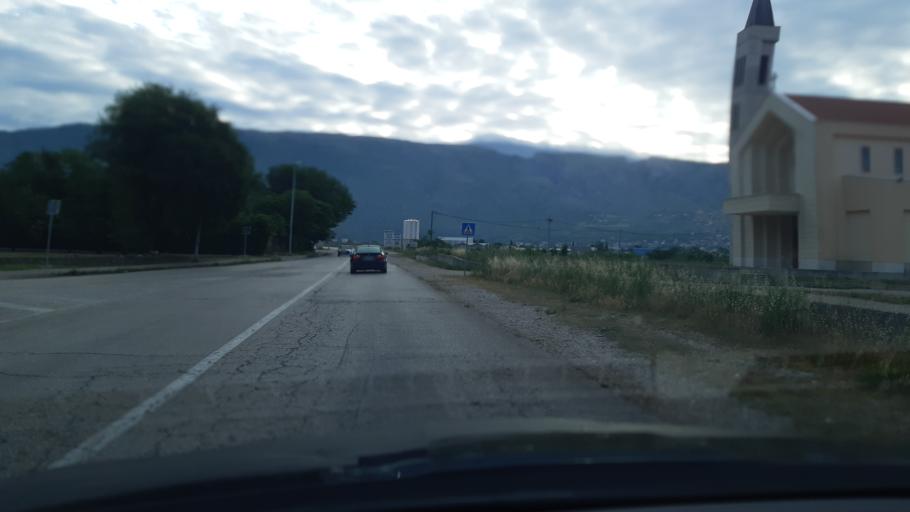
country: BA
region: Federation of Bosnia and Herzegovina
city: Rodoc
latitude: 43.3120
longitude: 17.8129
